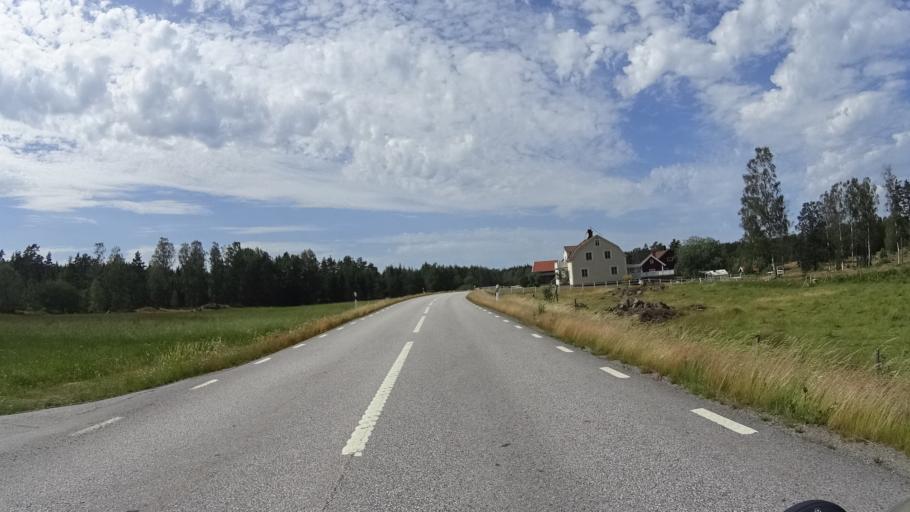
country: SE
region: OEstergoetland
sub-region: Atvidabergs Kommun
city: Atvidaberg
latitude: 58.0856
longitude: 16.1441
